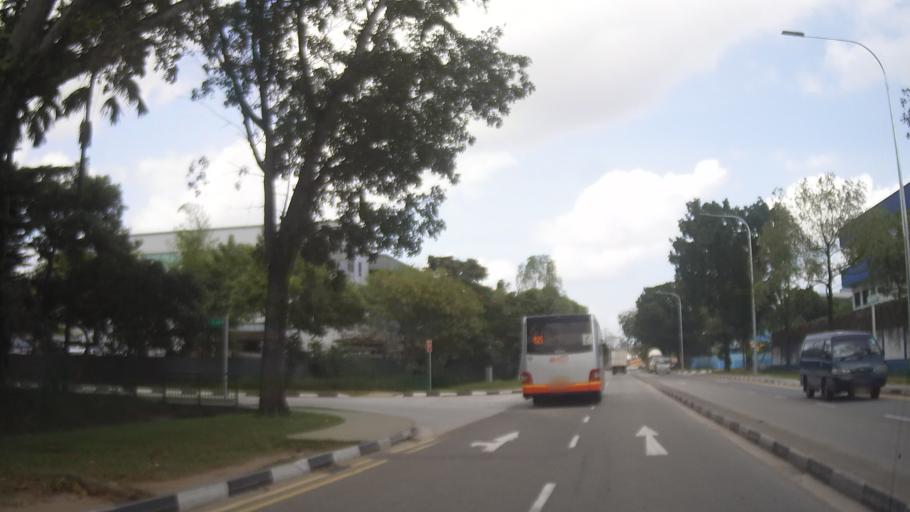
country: MY
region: Johor
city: Johor Bahru
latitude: 1.4324
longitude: 103.7478
